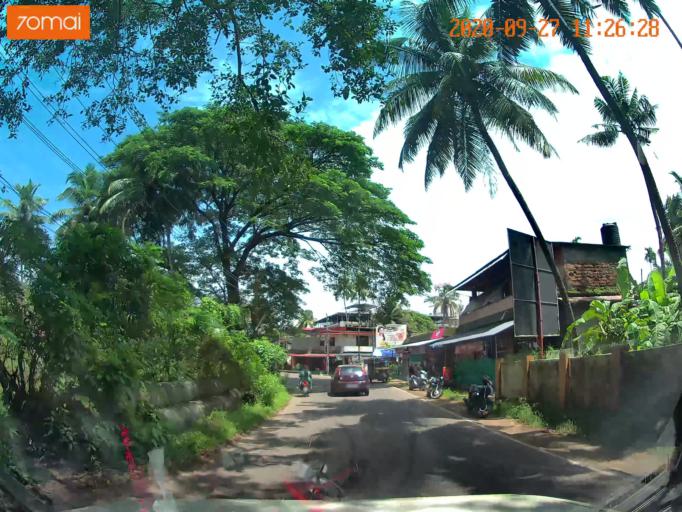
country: IN
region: Kerala
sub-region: Thrissur District
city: Thanniyam
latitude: 10.4159
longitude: 76.1541
